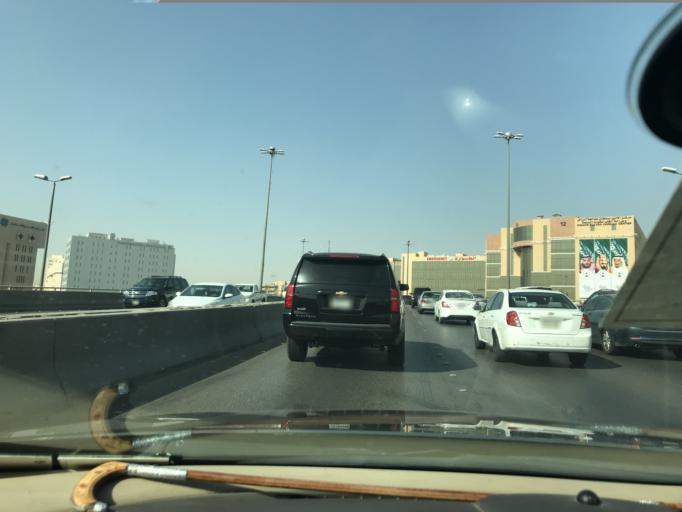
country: SA
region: Ar Riyad
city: Riyadh
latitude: 24.6927
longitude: 46.7191
